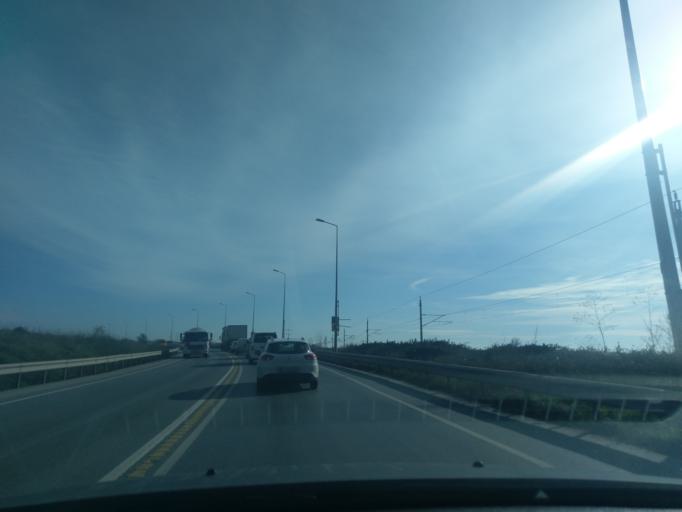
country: TR
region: Istanbul
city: Esenyurt
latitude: 41.0568
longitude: 28.7049
